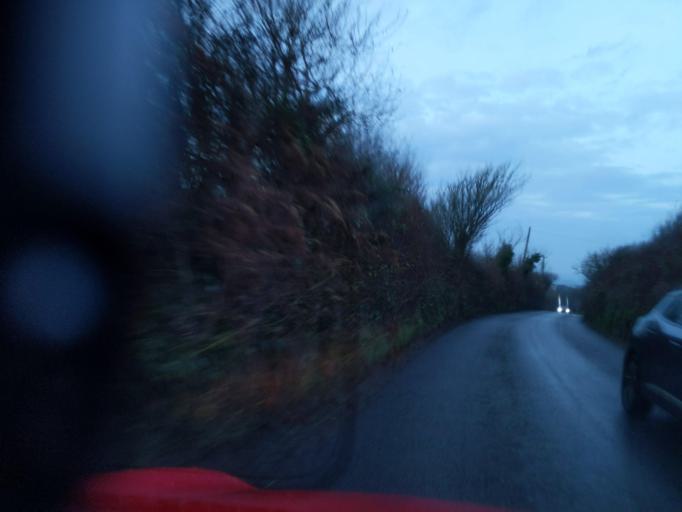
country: GB
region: England
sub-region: Plymouth
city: Plymstock
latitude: 50.3462
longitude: -4.0773
